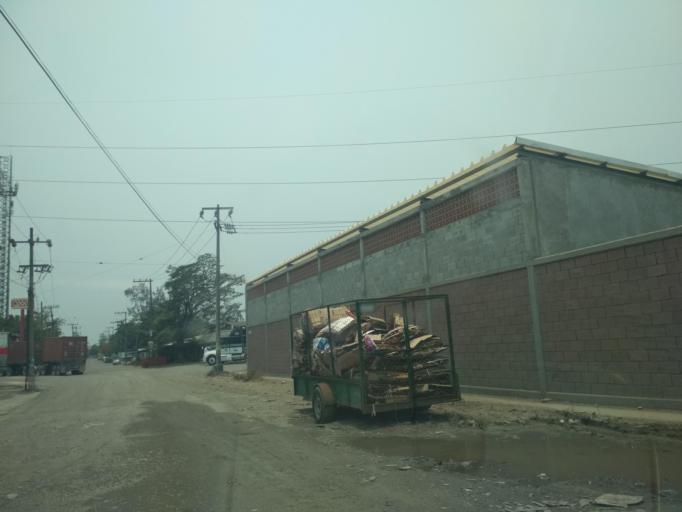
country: MX
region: Veracruz
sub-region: Veracruz
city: Lomas de Rio Medio Cuatro
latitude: 19.1699
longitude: -96.2331
